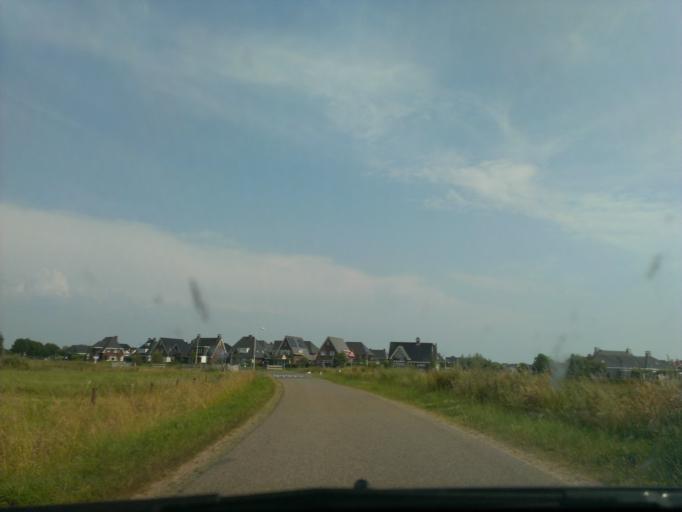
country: NL
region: Overijssel
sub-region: Gemeente Hof van Twente
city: Markelo
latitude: 52.3153
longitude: 6.4896
